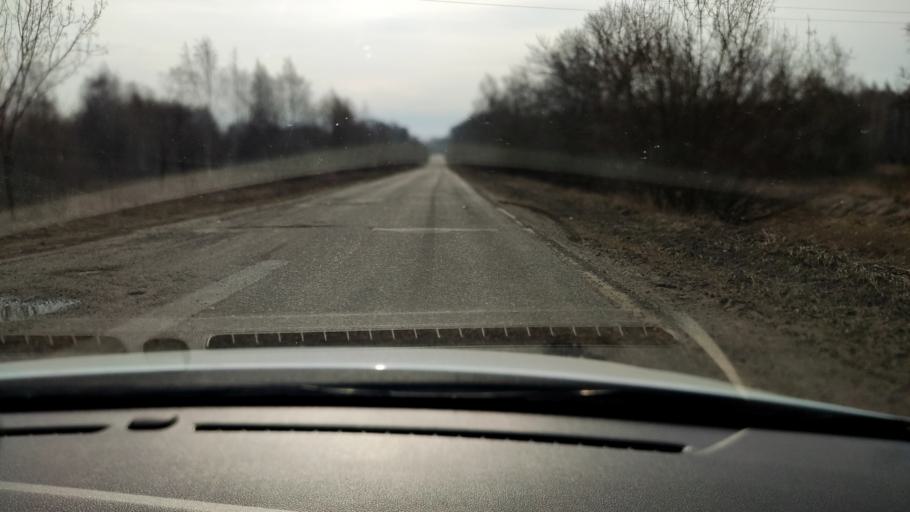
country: RU
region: Tatarstan
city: Stolbishchi
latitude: 55.7192
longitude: 49.2141
